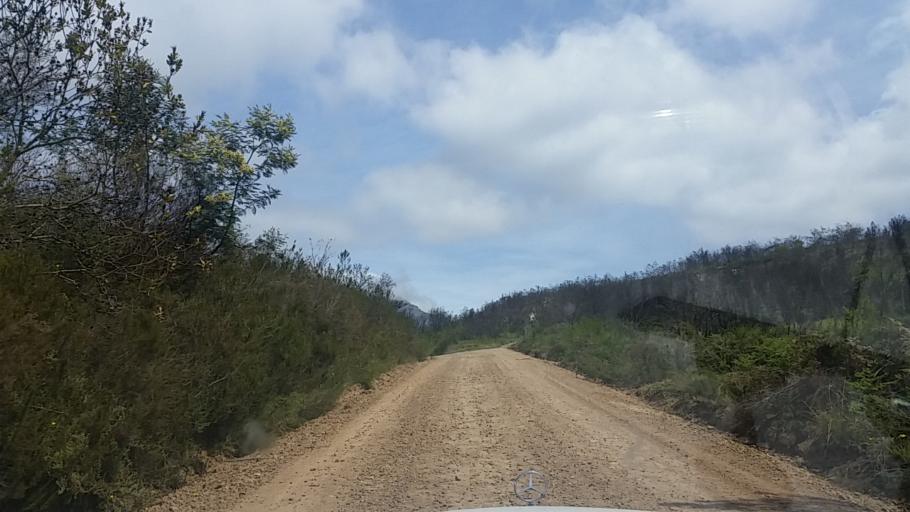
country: ZA
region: Western Cape
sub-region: Eden District Municipality
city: George
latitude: -33.8831
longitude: 22.4319
